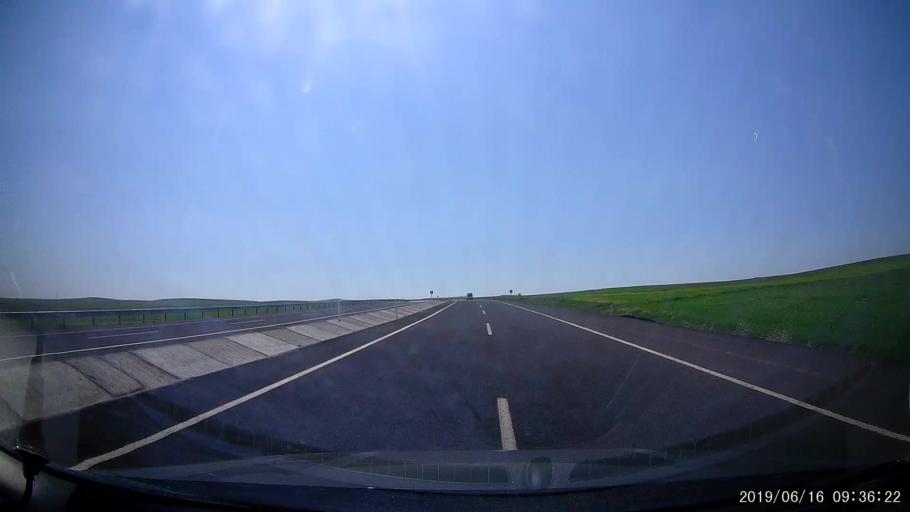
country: TR
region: Kars
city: Kars
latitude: 40.5585
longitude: 43.1713
